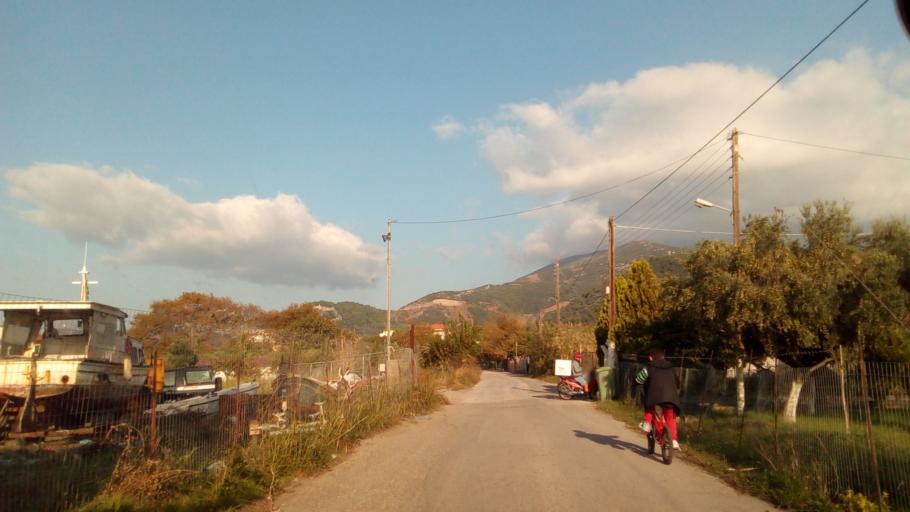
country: GR
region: West Greece
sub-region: Nomos Aitolias kai Akarnanias
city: Nafpaktos
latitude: 38.3879
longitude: 21.8472
